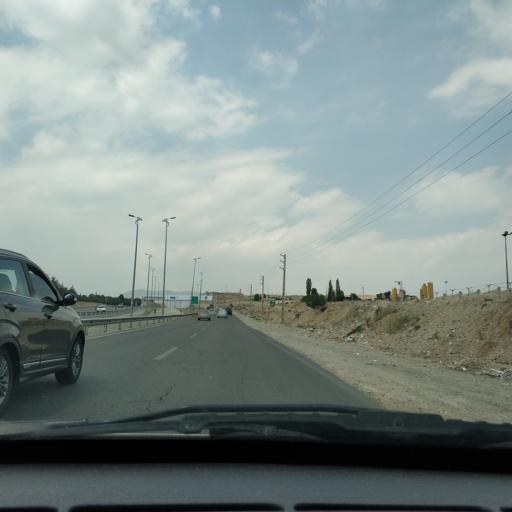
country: IR
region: Tehran
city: Tajrish
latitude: 35.7816
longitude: 51.5638
